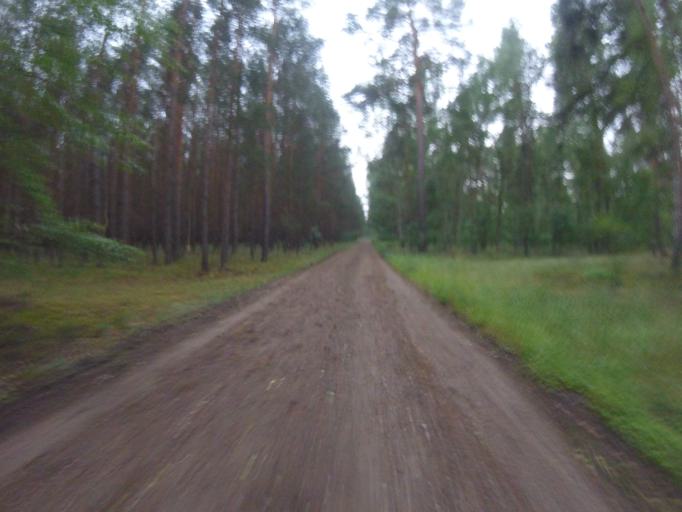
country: DE
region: Brandenburg
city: Gross Koris
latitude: 52.2009
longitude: 13.6970
